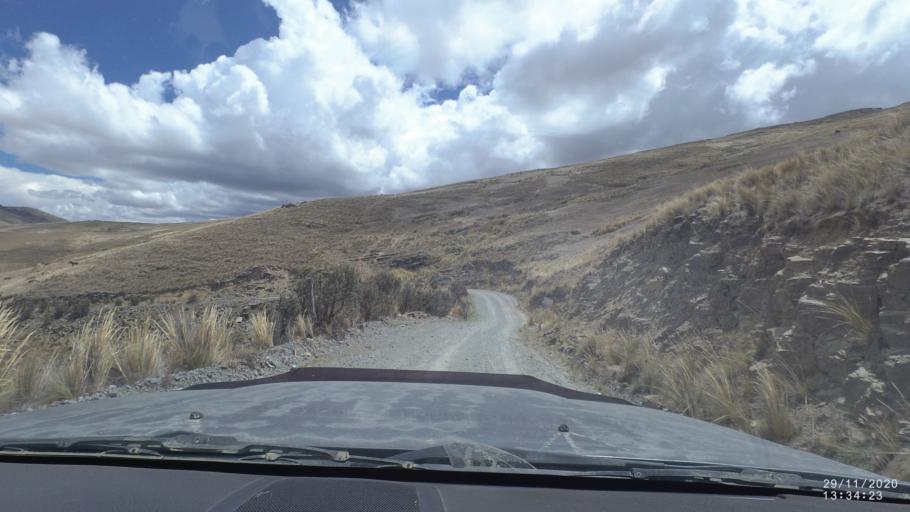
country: BO
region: Cochabamba
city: Cochabamba
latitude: -17.1108
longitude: -66.3363
